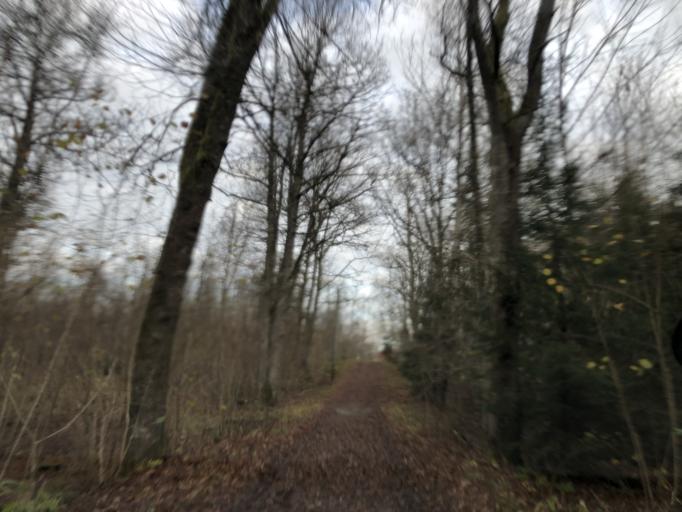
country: SE
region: Vaestra Goetaland
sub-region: Ulricehamns Kommun
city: Ulricehamn
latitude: 57.7228
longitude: 13.3083
